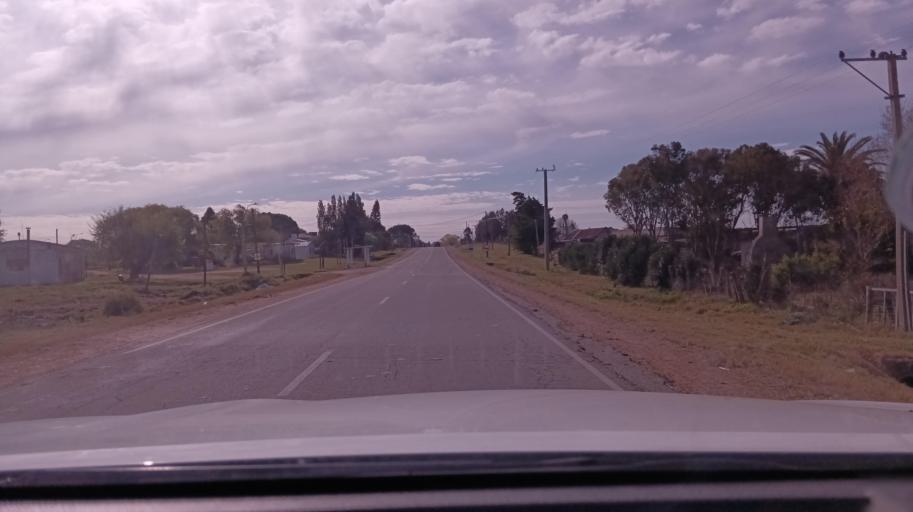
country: UY
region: Canelones
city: Toledo
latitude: -34.7251
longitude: -56.1131
